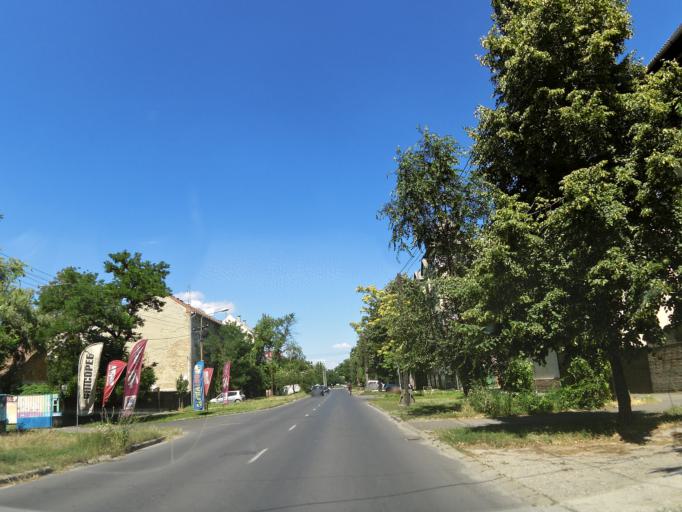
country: HU
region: Csongrad
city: Szeged
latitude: 46.2648
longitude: 20.1370
